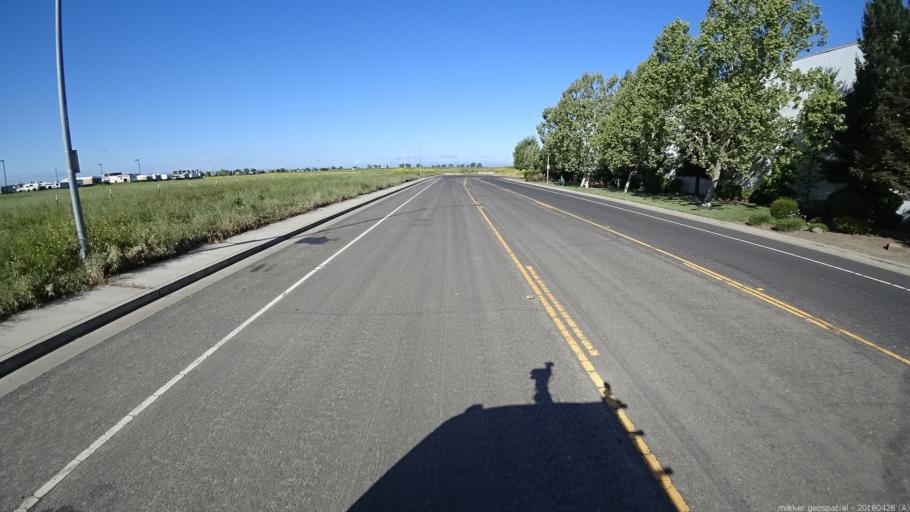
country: US
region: California
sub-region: Yolo County
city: West Sacramento
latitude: 38.5471
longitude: -121.5719
